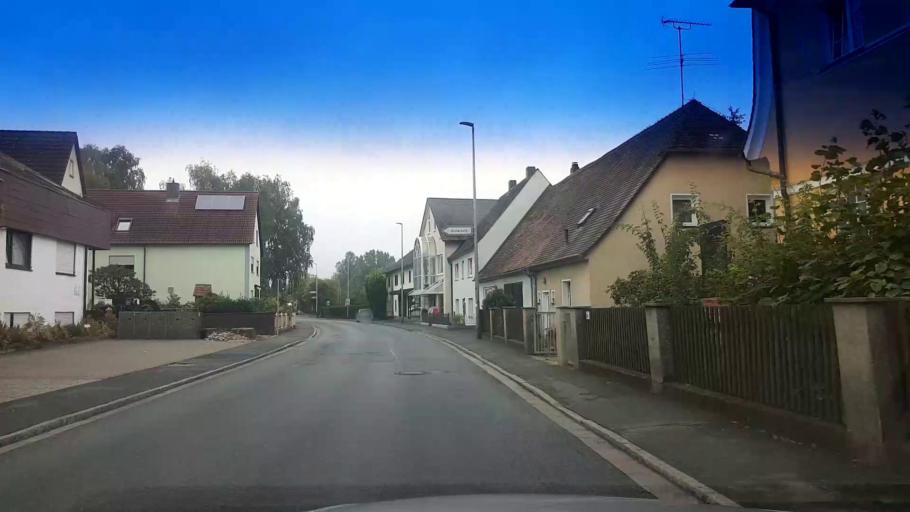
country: DE
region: Bavaria
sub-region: Upper Franconia
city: Heroldsbach
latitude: 49.6922
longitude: 11.0003
